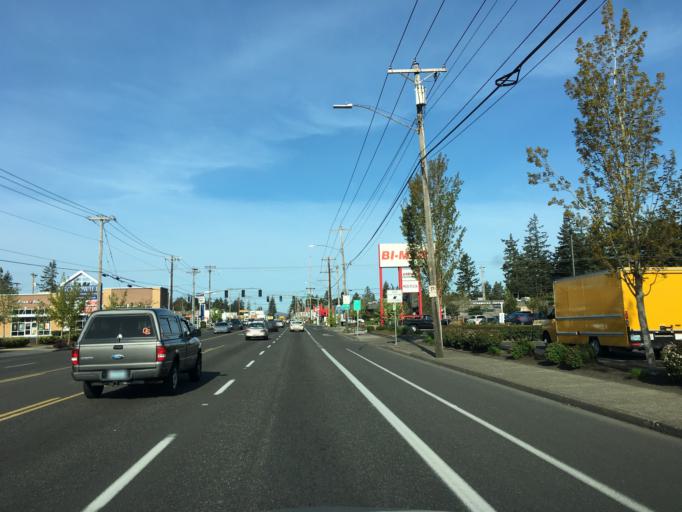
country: US
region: Oregon
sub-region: Multnomah County
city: Lents
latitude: 45.5336
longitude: -122.5359
